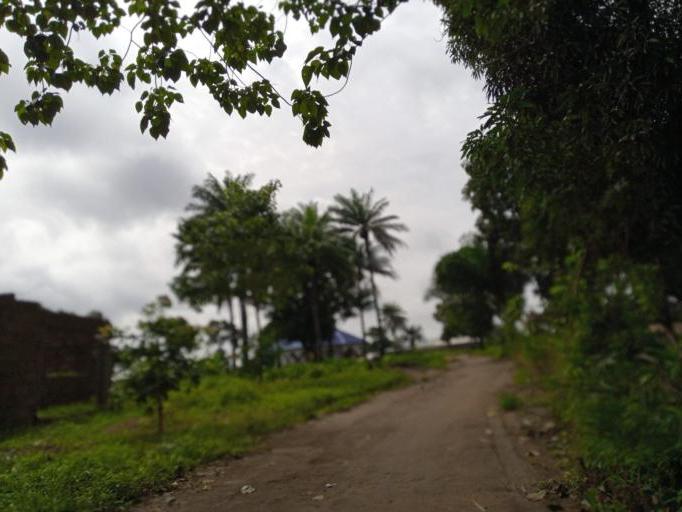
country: SL
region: Northern Province
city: Sawkta
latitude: 8.6272
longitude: -13.2006
